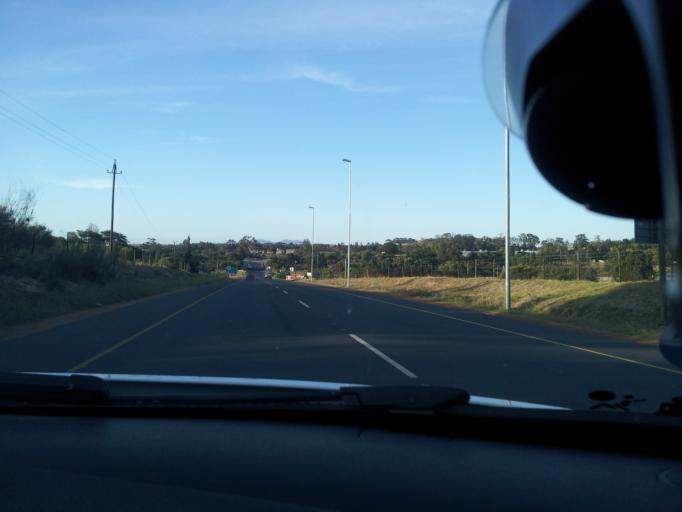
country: ZA
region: Western Cape
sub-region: Cape Winelands District Municipality
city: Paarl
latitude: -33.8027
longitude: 18.8721
